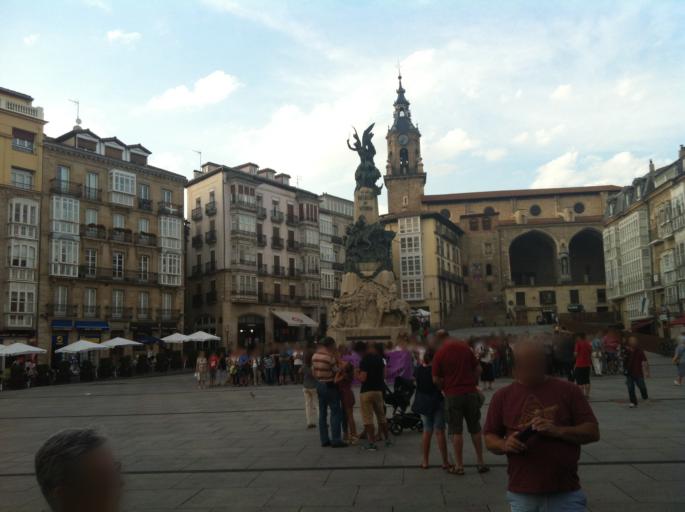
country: ES
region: Basque Country
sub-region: Provincia de Alava
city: Gasteiz / Vitoria
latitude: 42.8462
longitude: -2.6734
